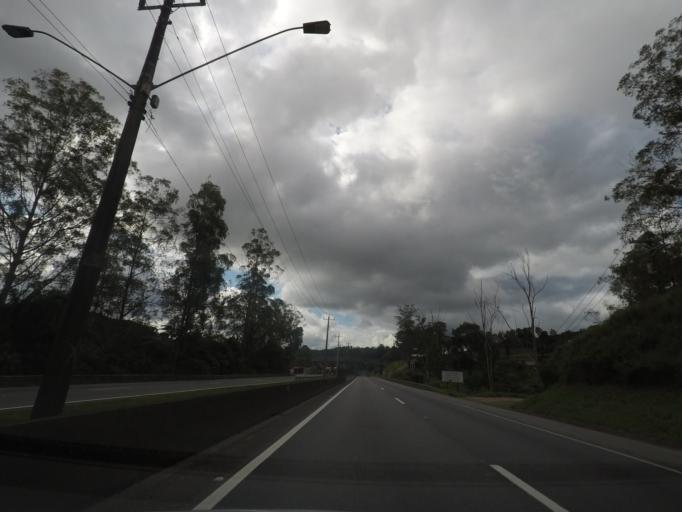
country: BR
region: Sao Paulo
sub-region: Sao Lourenco Da Serra
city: Sao Lourenco da Serra
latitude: -23.8538
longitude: -46.9396
